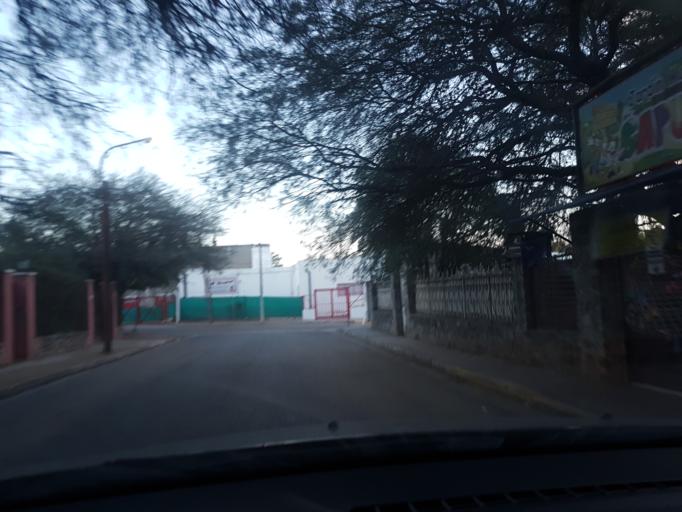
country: AR
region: Cordoba
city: Villa Allende
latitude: -31.2888
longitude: -64.2972
